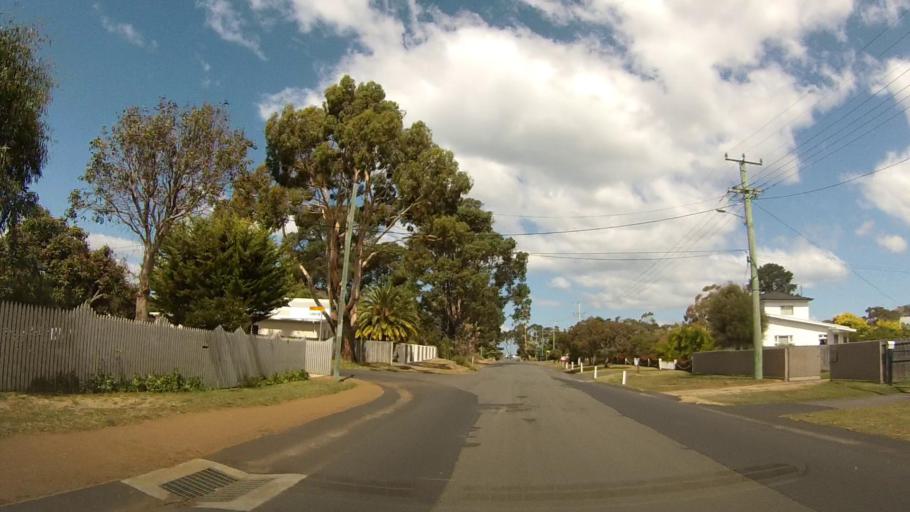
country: AU
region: Tasmania
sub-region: Clarence
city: Seven Mile Beach
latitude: -42.8600
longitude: 147.5028
